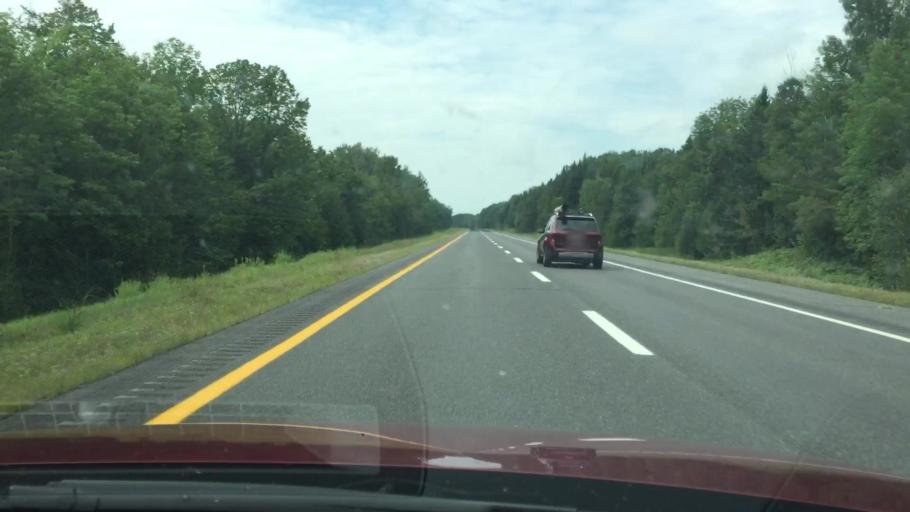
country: US
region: Maine
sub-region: Aroostook County
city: Houlton
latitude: 46.1393
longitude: -67.9218
